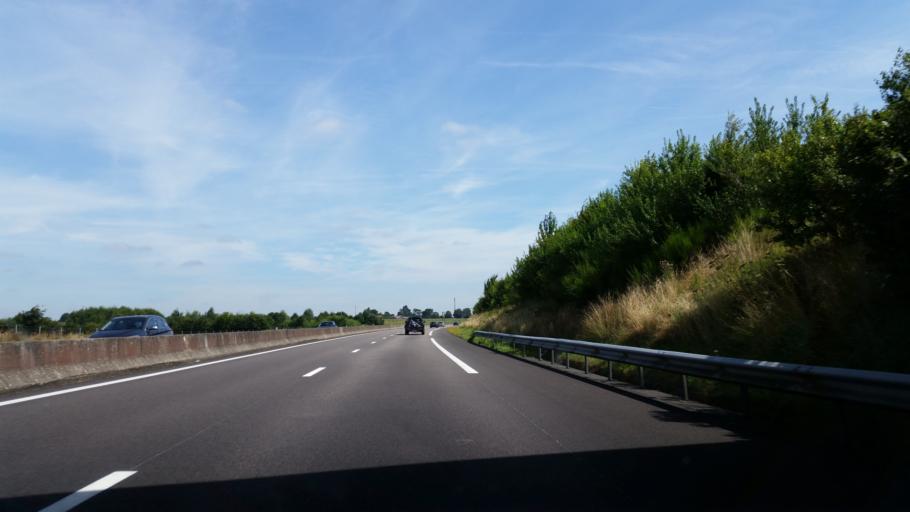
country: FR
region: Haute-Normandie
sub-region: Departement de la Seine-Maritime
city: Aumale
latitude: 49.7739
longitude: 1.7173
